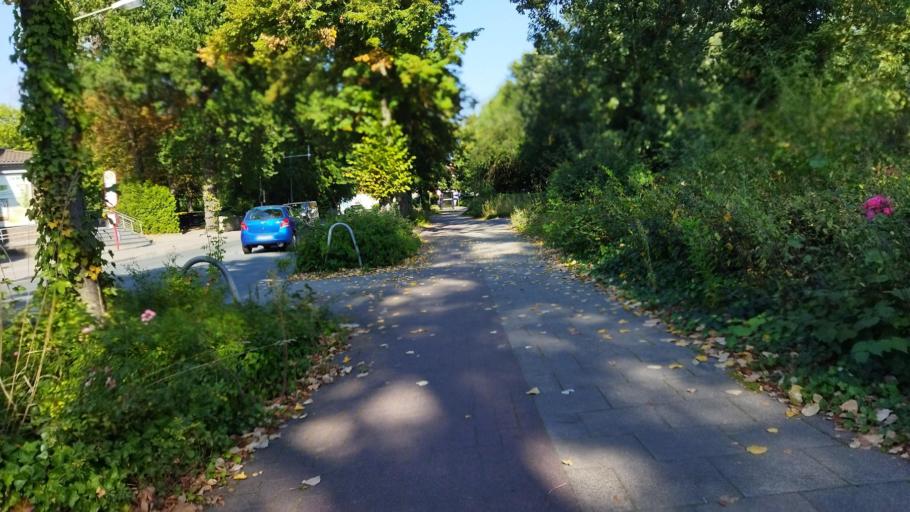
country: DE
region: Lower Saxony
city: Osnabrueck
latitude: 52.2708
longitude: 8.0066
